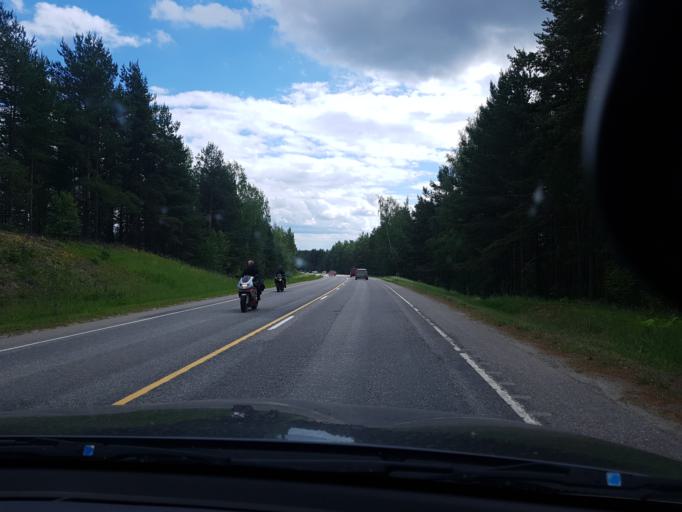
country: FI
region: Pirkanmaa
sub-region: Tampere
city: Paelkaene
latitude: 61.3123
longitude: 24.2875
